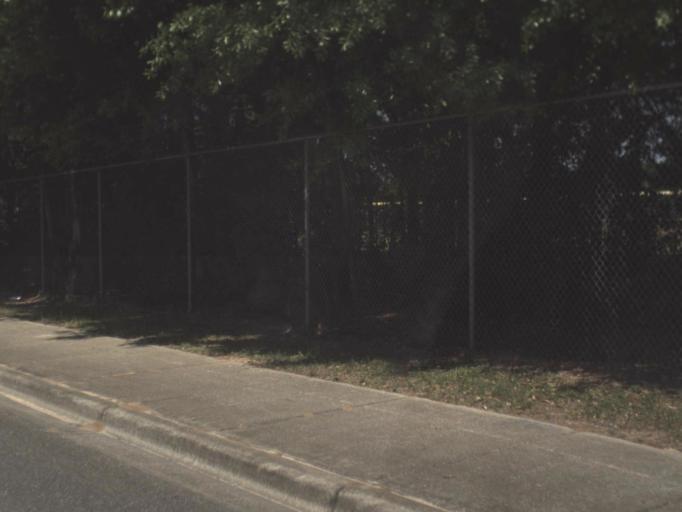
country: US
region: Florida
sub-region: Escambia County
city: Brent
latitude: 30.4783
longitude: -87.2393
